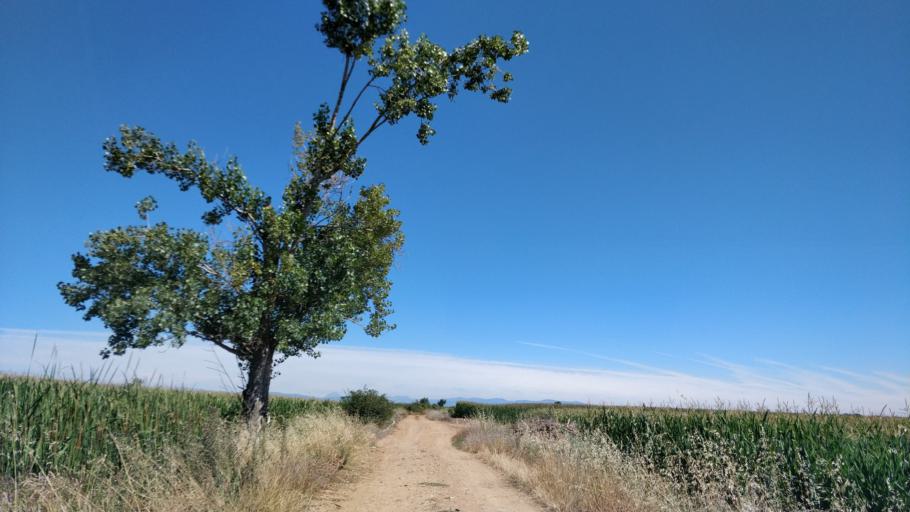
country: ES
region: Castille and Leon
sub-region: Provincia de Leon
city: Bustillo del Paramo
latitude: 42.4421
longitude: -5.8151
